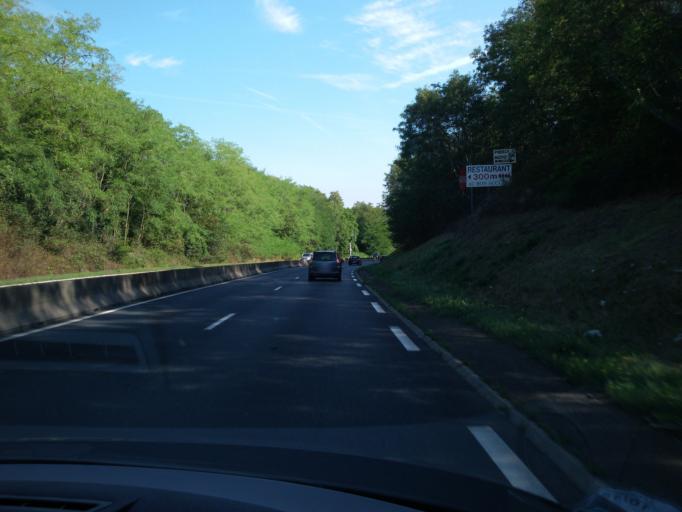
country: FR
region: Ile-de-France
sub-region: Departement de l'Essonne
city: Boissy-sous-Saint-Yon
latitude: 48.5382
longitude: 2.2096
